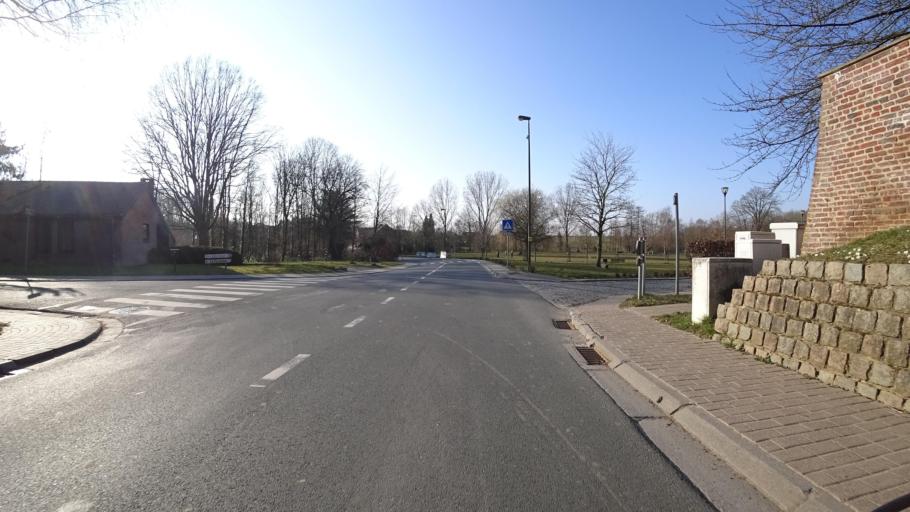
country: BE
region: Wallonia
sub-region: Province du Brabant Wallon
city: Chastre-Villeroux-Blanmont
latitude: 50.6103
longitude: 4.6438
